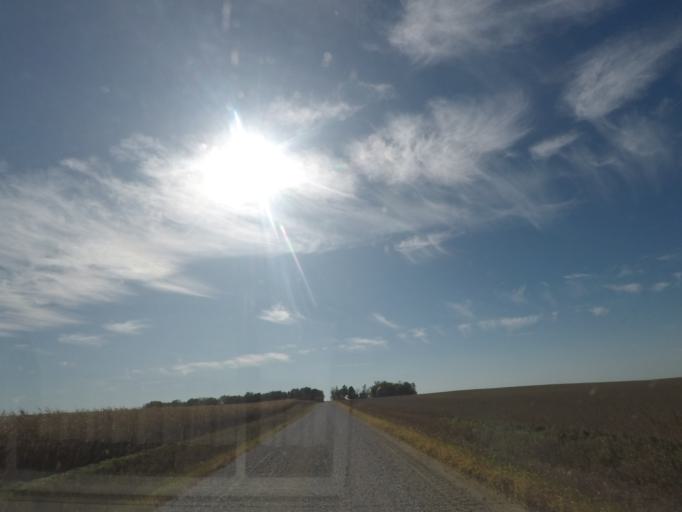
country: US
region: Iowa
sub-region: Story County
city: Nevada
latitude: 42.0538
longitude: -93.3291
